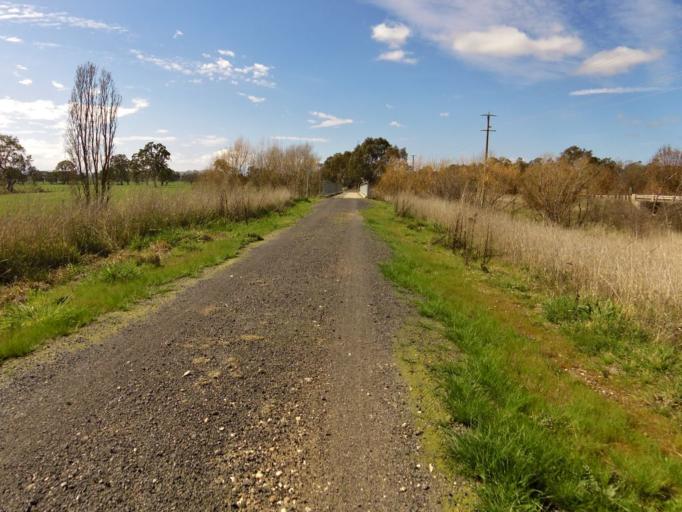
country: AU
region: Victoria
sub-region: Mansfield
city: Mansfield
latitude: -37.0443
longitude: 146.0447
